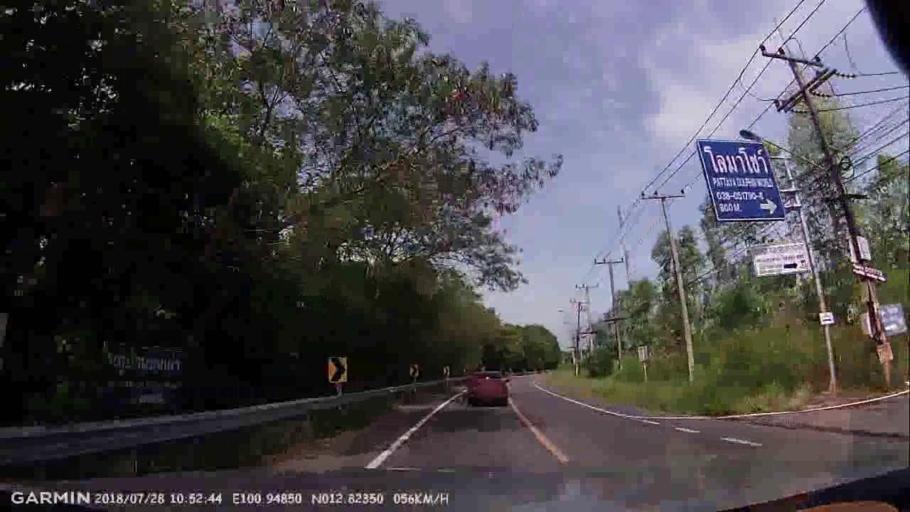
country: TH
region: Chon Buri
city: Phatthaya
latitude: 12.8234
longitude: 100.9484
